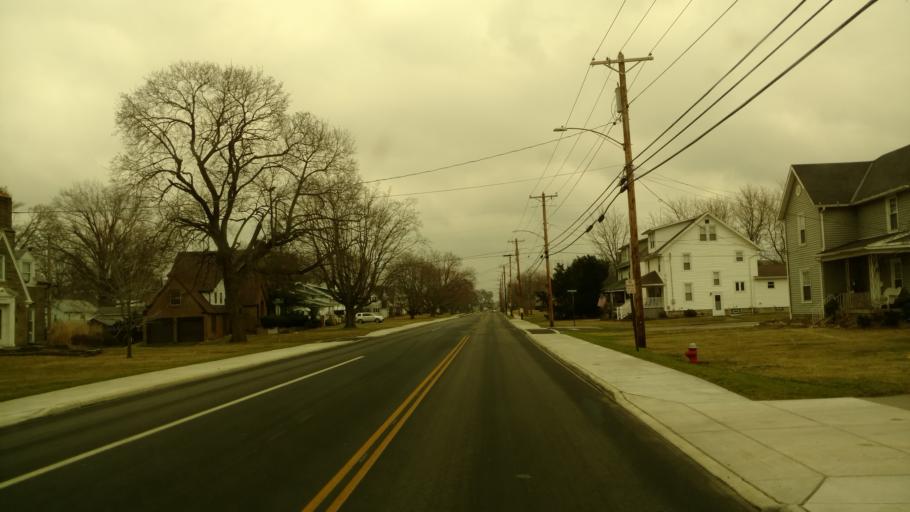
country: US
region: Ohio
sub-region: Richland County
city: Shelby
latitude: 40.8771
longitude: -82.6542
